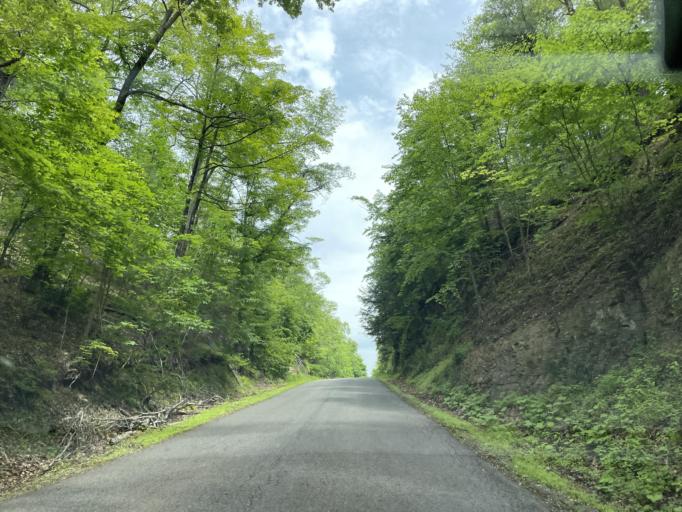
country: US
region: New York
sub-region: Ulster County
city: West Hurley
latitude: 41.9717
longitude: -74.0696
